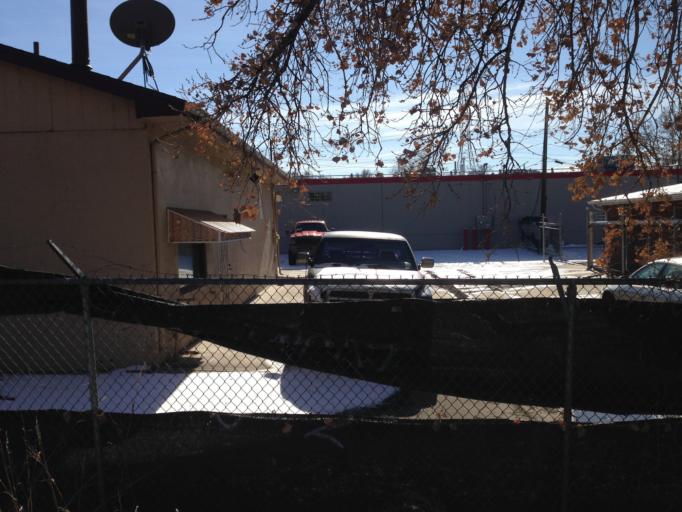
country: US
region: Colorado
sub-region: Adams County
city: Berkley
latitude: 39.7963
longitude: -105.0433
